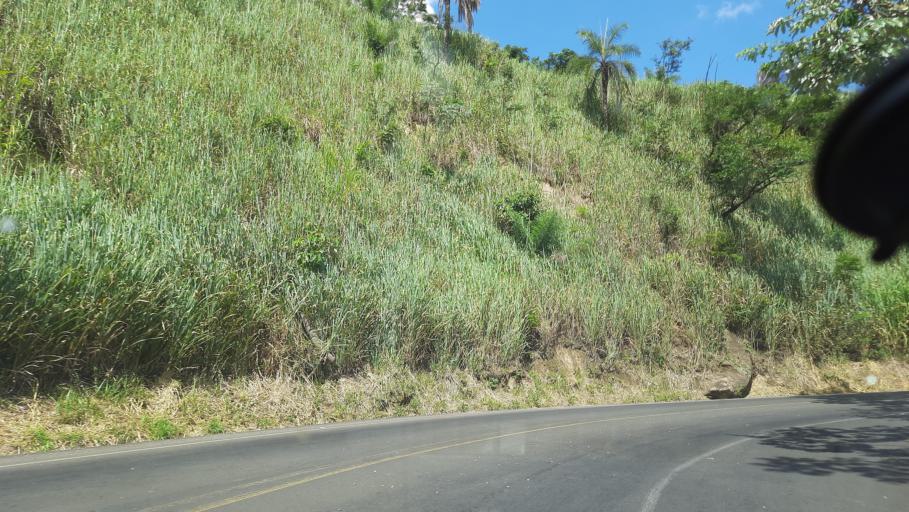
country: BR
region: Sao Paulo
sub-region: Sao Jose Do Rio Pardo
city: Sao Jose do Rio Pardo
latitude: -21.5983
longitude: -46.9368
